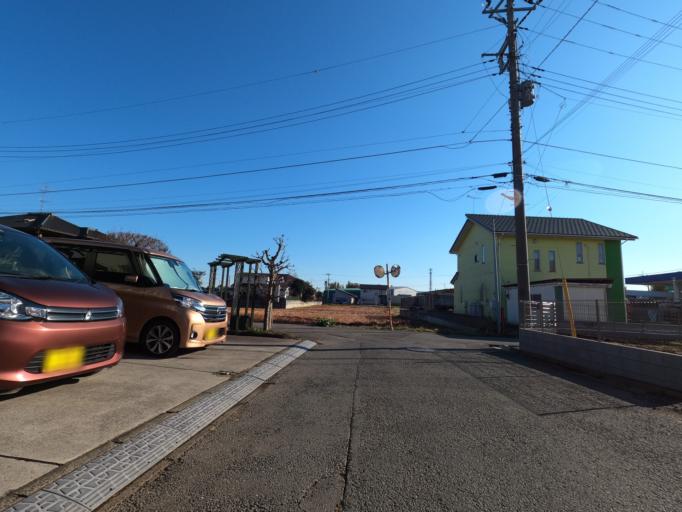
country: JP
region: Ibaraki
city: Moriya
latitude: 35.9616
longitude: 139.9752
